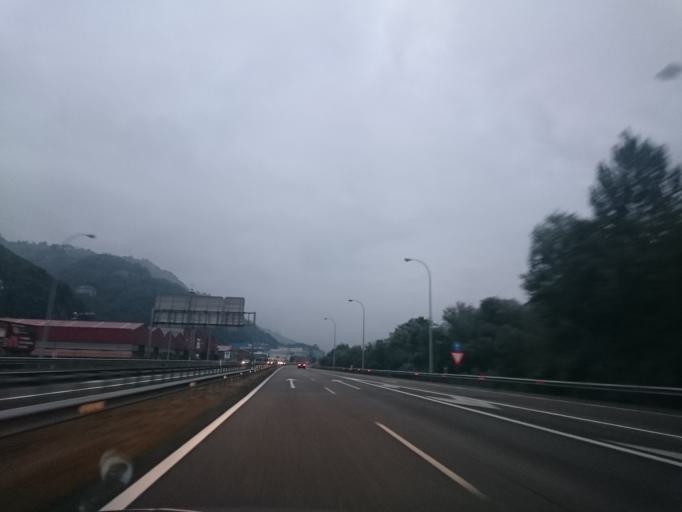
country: ES
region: Asturias
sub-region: Province of Asturias
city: Mieres
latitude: 43.2360
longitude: -5.7803
